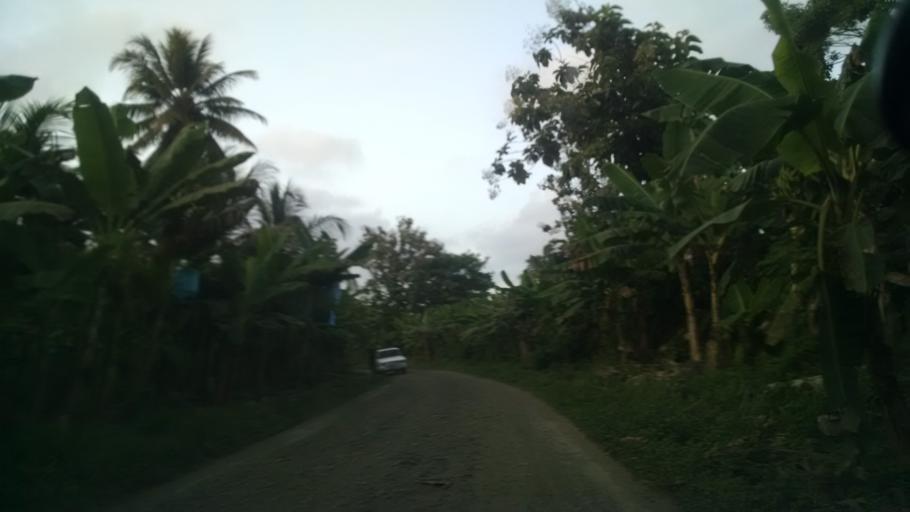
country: CO
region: Antioquia
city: San Juan de Uraba
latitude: 8.7308
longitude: -76.6052
